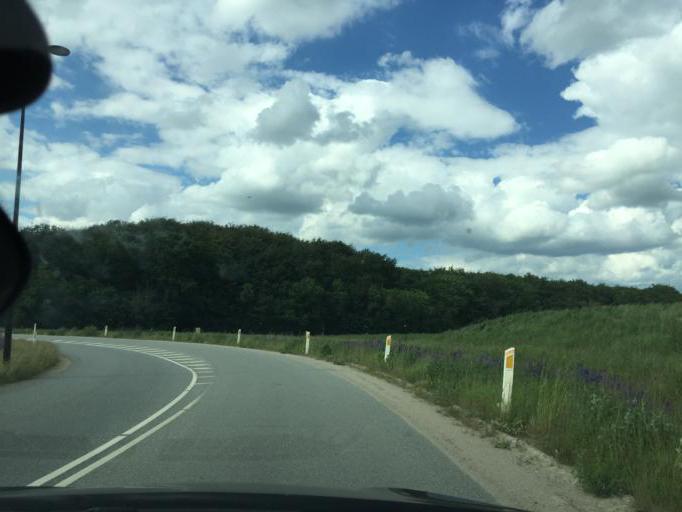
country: DK
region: South Denmark
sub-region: Odense Kommune
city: Neder Holluf
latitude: 55.3698
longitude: 10.4231
